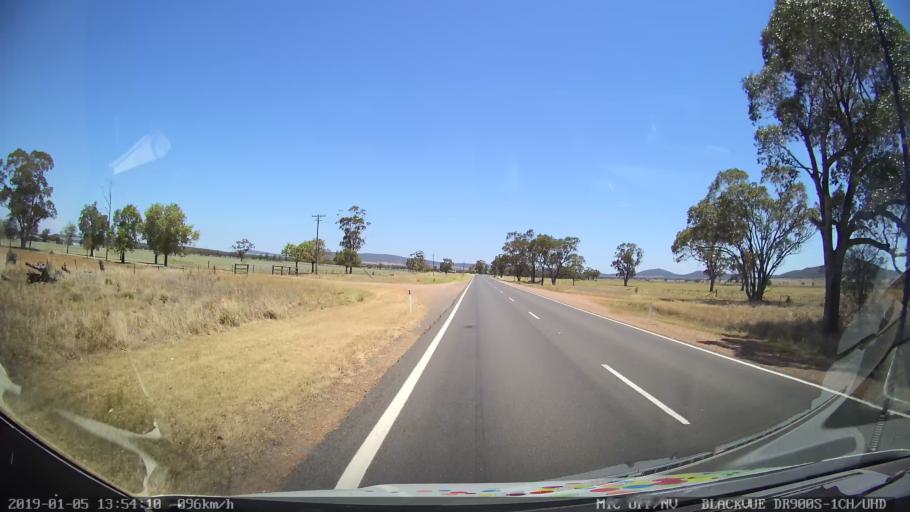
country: AU
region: New South Wales
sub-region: Gunnedah
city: Gunnedah
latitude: -31.0850
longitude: 150.2749
